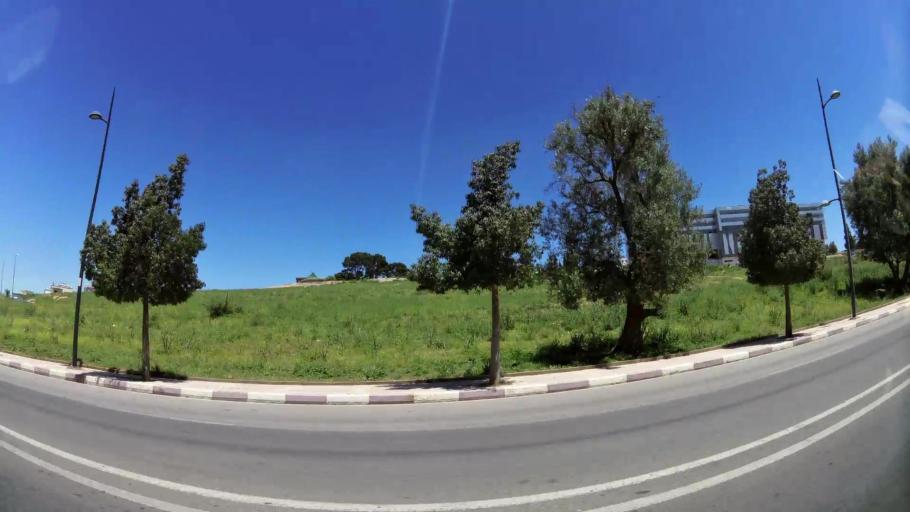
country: MA
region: Meknes-Tafilalet
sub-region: Meknes
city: Meknes
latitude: 33.9037
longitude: -5.5556
